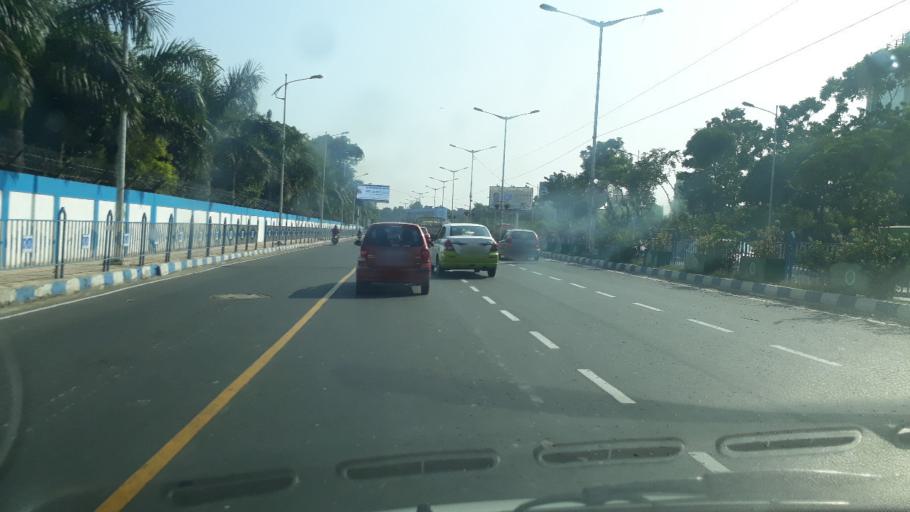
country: IN
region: West Bengal
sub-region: Kolkata
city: Kolkata
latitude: 22.5646
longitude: 88.4072
